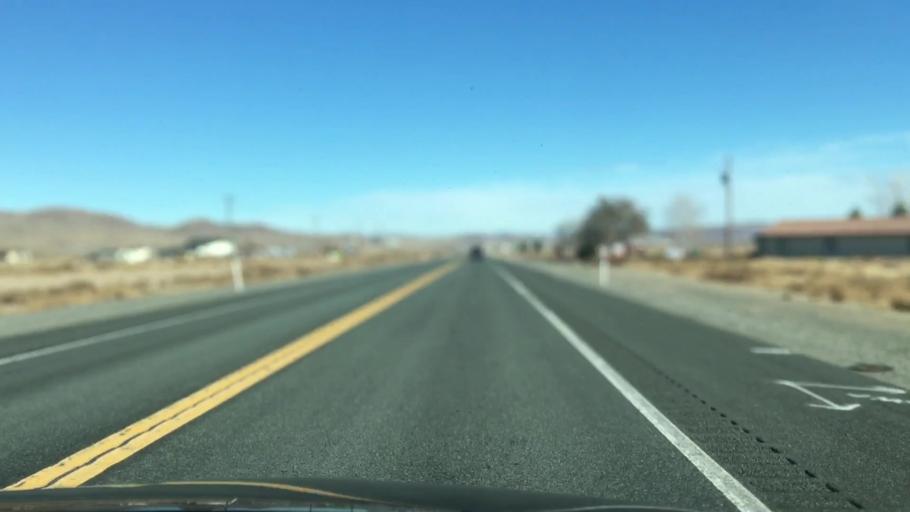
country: US
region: Nevada
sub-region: Lyon County
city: Silver Springs
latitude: 39.3956
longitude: -119.2812
